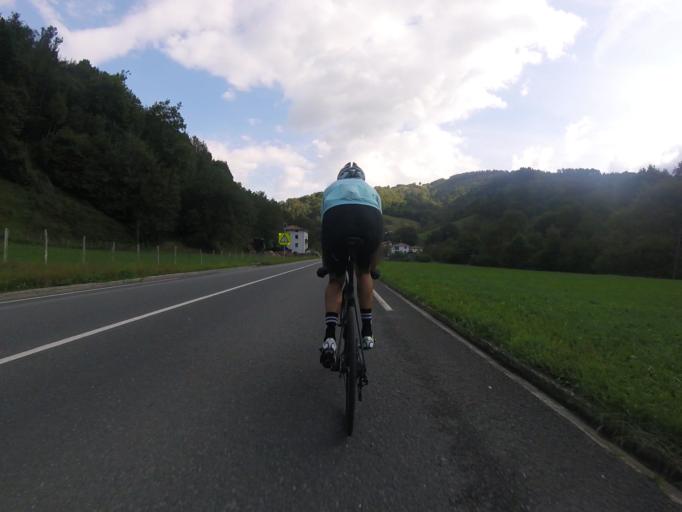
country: ES
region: Basque Country
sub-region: Provincia de Guipuzcoa
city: Amezqueta
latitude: 43.0669
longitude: -2.0852
